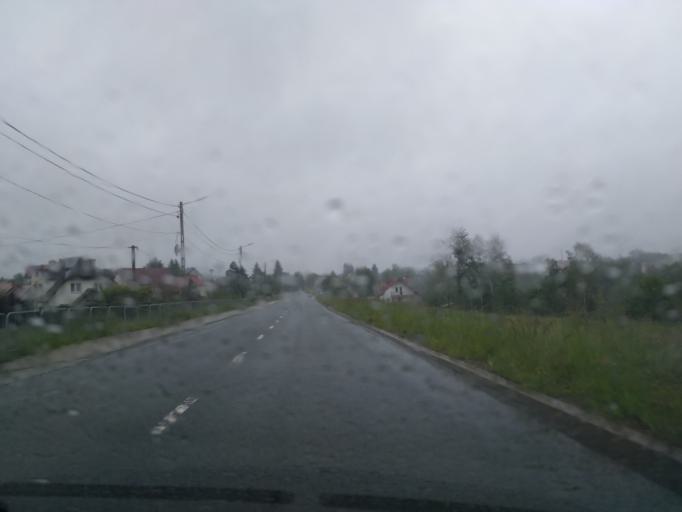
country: PL
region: Lesser Poland Voivodeship
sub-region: Powiat gorlicki
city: Gorlice
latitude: 49.6763
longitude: 21.1585
